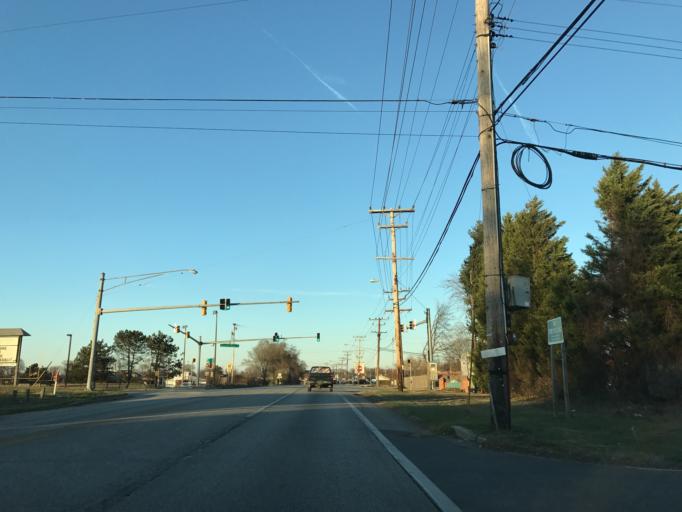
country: US
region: Maryland
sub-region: Anne Arundel County
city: Riviera Beach
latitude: 39.1502
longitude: -76.5218
